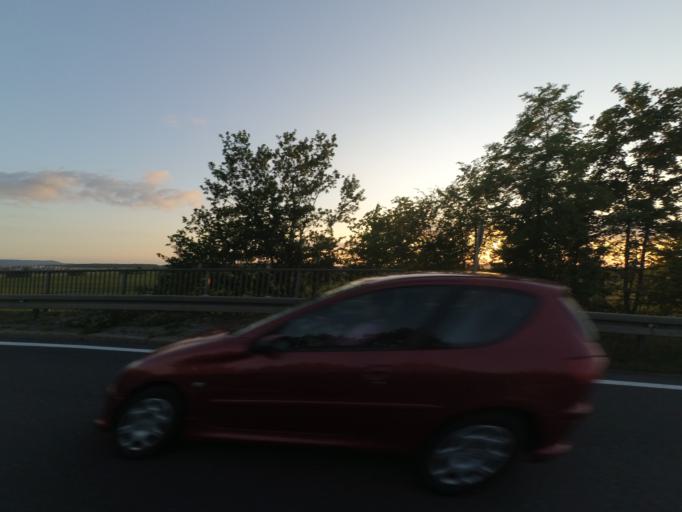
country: DE
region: Bavaria
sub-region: Regierungsbezirk Unterfranken
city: Zeil
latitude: 50.0164
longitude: 10.5645
